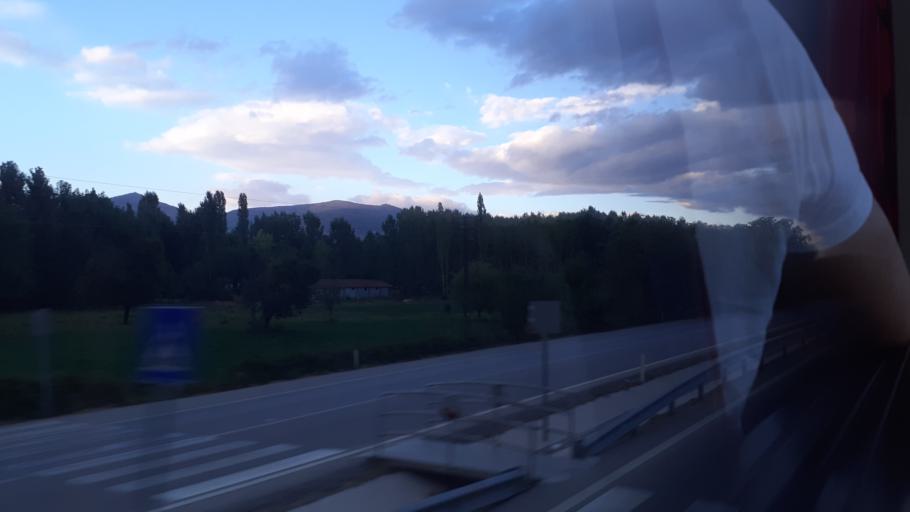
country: TR
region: Tokat
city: Dokmetepe
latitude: 40.3217
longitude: 36.2106
